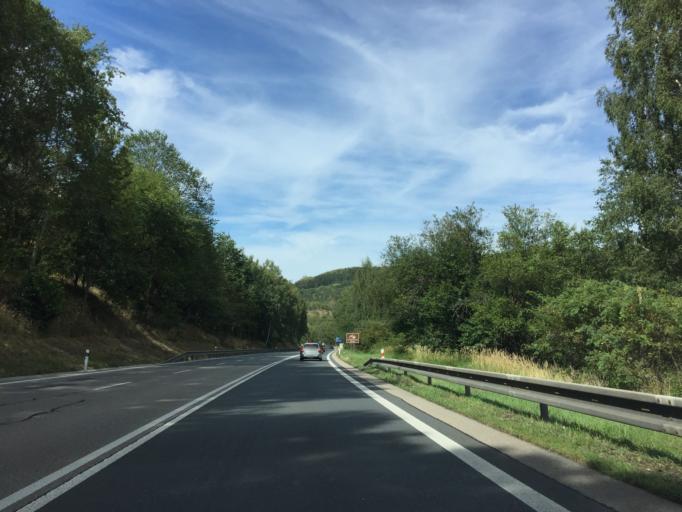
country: CZ
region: Central Bohemia
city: Votice
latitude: 49.6321
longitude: 14.6510
